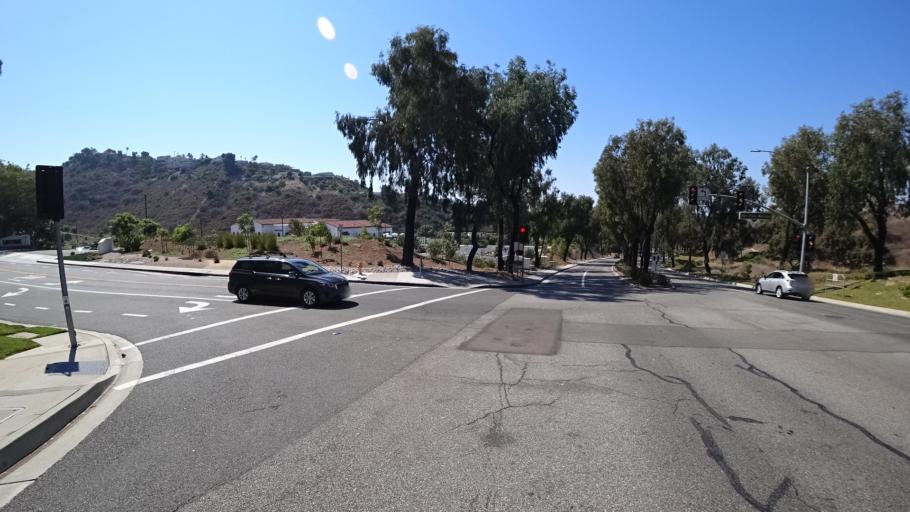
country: US
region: California
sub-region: Orange County
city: San Clemente
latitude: 33.4431
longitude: -117.6066
